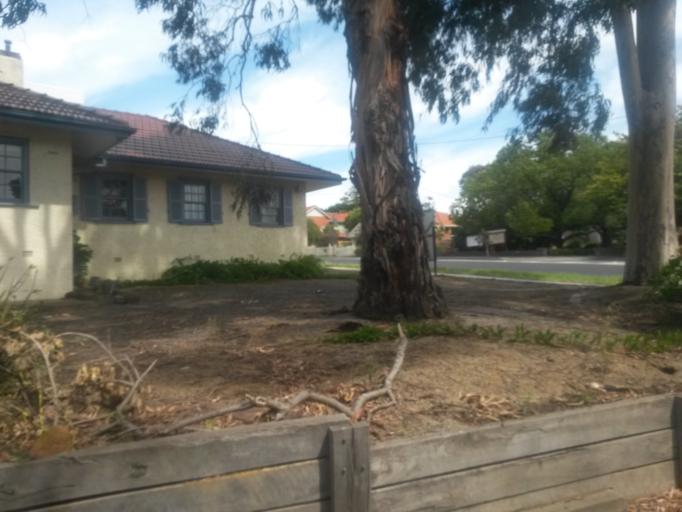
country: AU
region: Victoria
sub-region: Stonnington
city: Glen Iris
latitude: -37.8548
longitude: 145.0525
